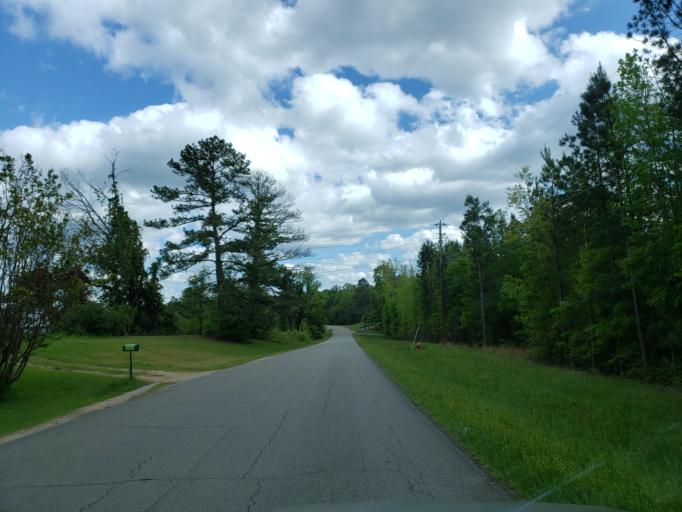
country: US
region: Georgia
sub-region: Haralson County
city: Tallapoosa
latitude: 33.7426
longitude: -85.3902
